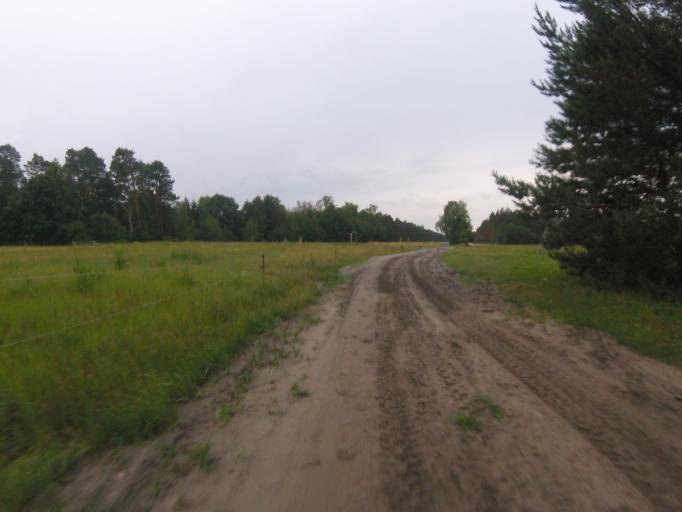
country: DE
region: Brandenburg
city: Gross Koris
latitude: 52.1946
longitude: 13.6461
